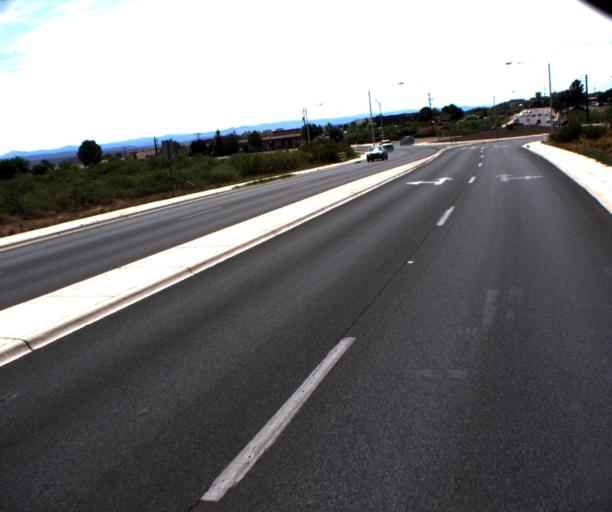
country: US
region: Arizona
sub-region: Yavapai County
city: Cottonwood
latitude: 34.7408
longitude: -112.0383
